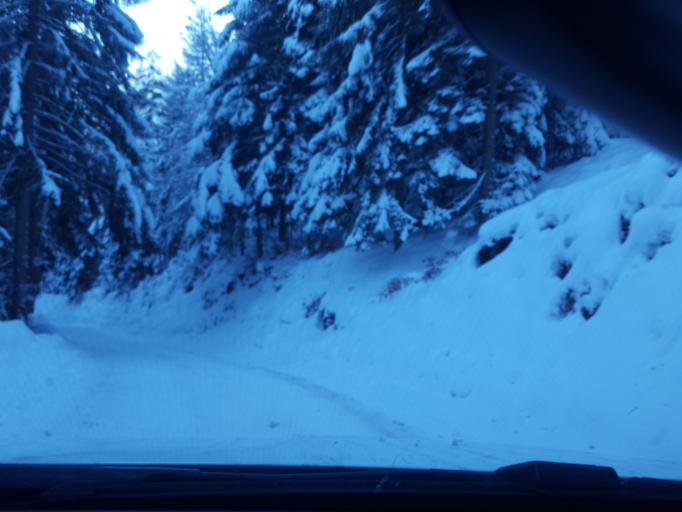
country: FR
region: Rhone-Alpes
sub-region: Departement de la Savoie
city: Salins-les-Thermes
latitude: 45.4748
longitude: 6.5137
